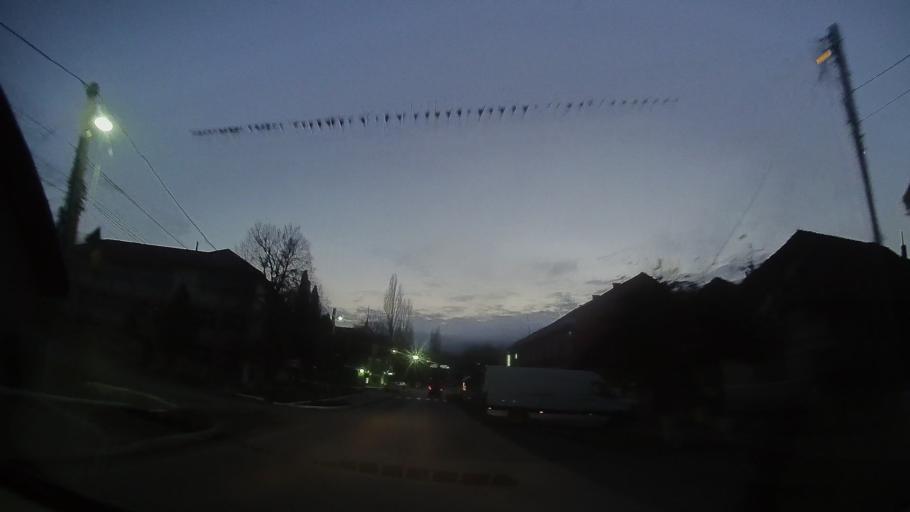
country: RO
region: Mures
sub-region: Comuna Sarmasu
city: Sarmasu
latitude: 46.7540
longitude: 24.1625
